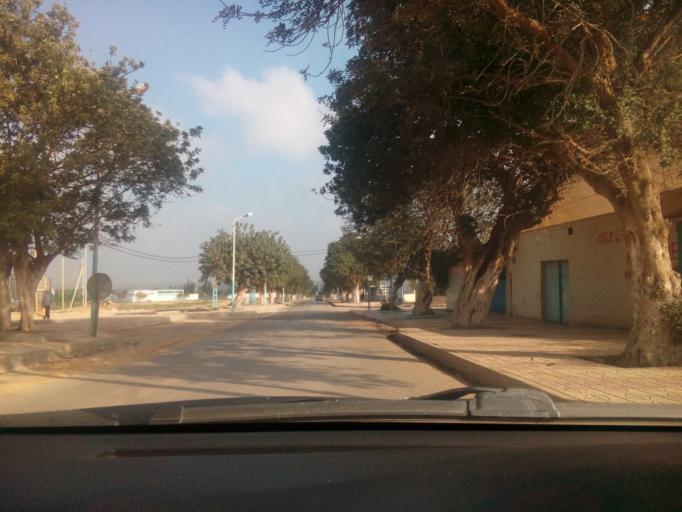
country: DZ
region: Oran
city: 'Ain el Turk
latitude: 35.7044
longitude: -0.8080
